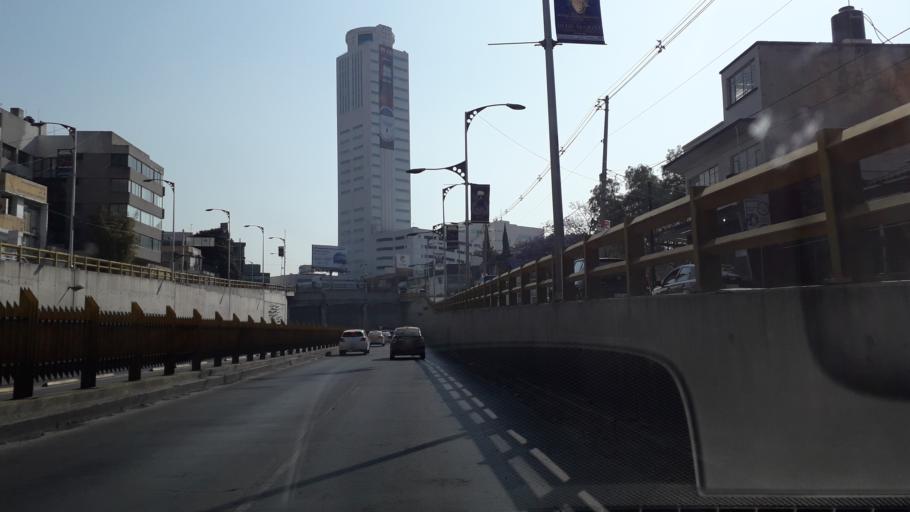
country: MX
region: Puebla
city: Puebla
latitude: 19.0521
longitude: -98.2246
